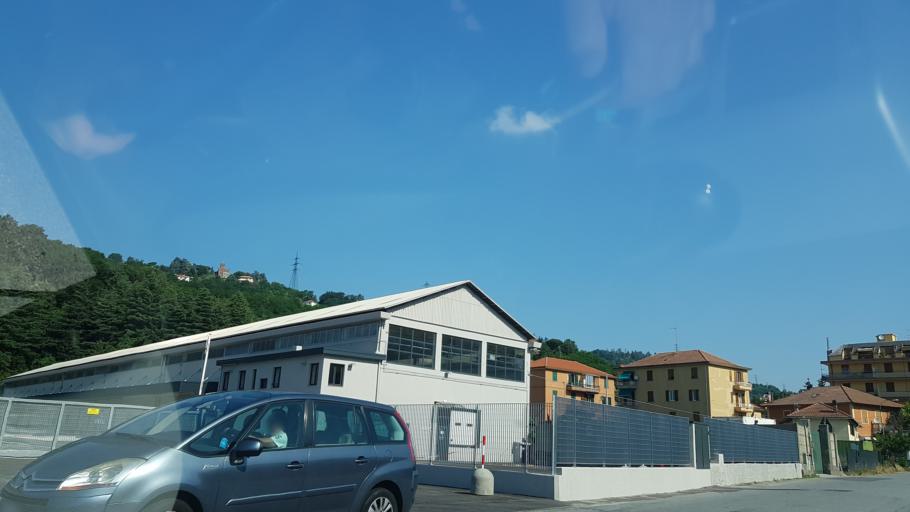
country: IT
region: Liguria
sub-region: Provincia di Genova
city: Manesseno
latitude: 44.4888
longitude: 8.9216
